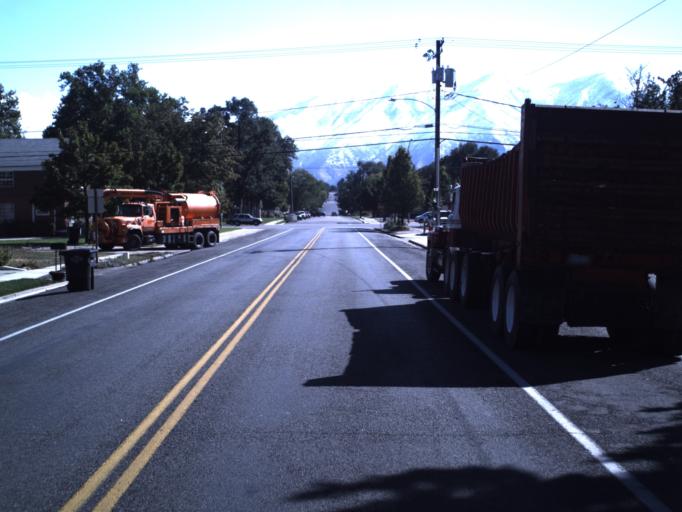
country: US
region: Utah
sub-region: Utah County
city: Spanish Fork
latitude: 40.1085
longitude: -111.6564
